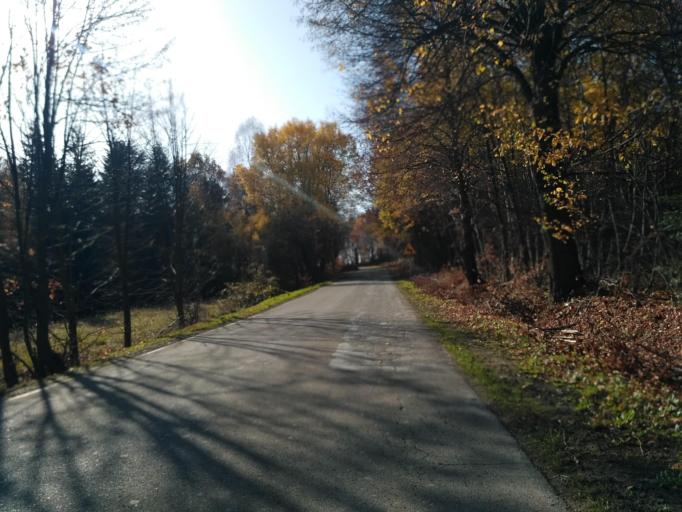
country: PL
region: Subcarpathian Voivodeship
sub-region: Powiat brzozowski
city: Wesola
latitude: 49.8373
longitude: 22.1507
